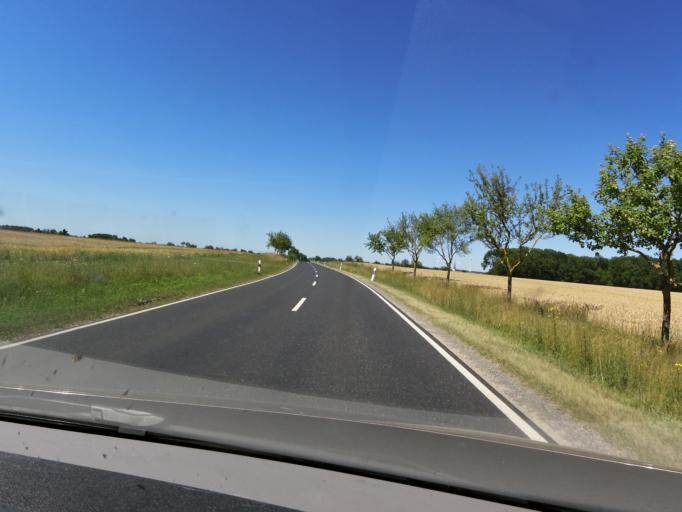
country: DE
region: Bavaria
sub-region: Regierungsbezirk Unterfranken
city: Biebelried
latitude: 49.7184
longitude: 10.0828
